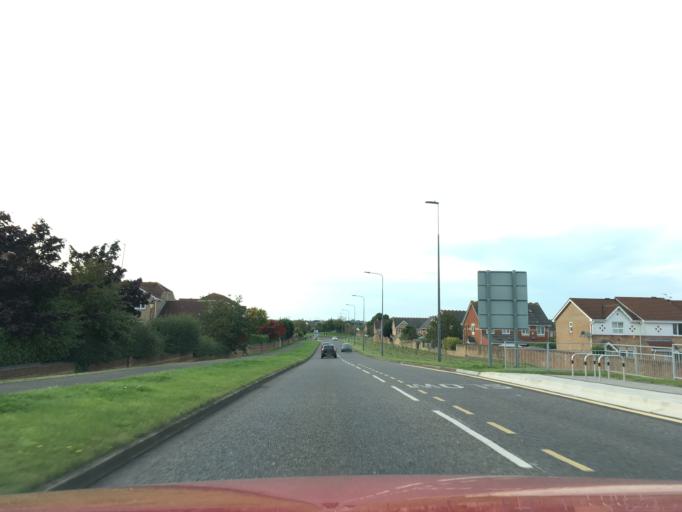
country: GB
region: England
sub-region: South Gloucestershire
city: Stoke Gifford
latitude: 51.5258
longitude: -2.5346
